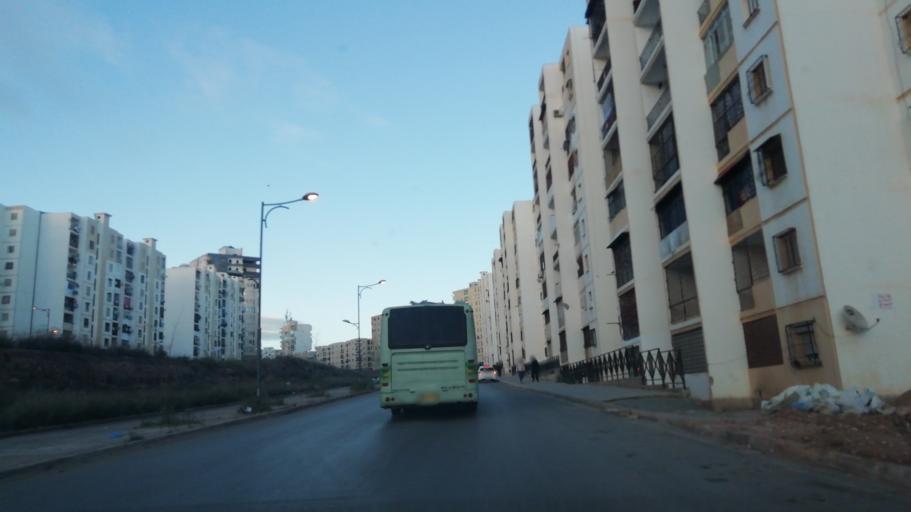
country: DZ
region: Oran
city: Bir el Djir
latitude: 35.6987
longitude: -0.5632
